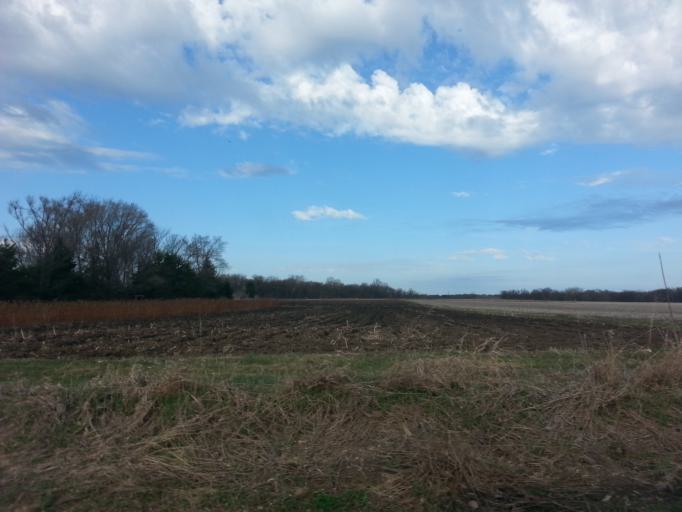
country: US
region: Minnesota
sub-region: Dakota County
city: Hastings
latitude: 44.7574
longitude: -92.8326
